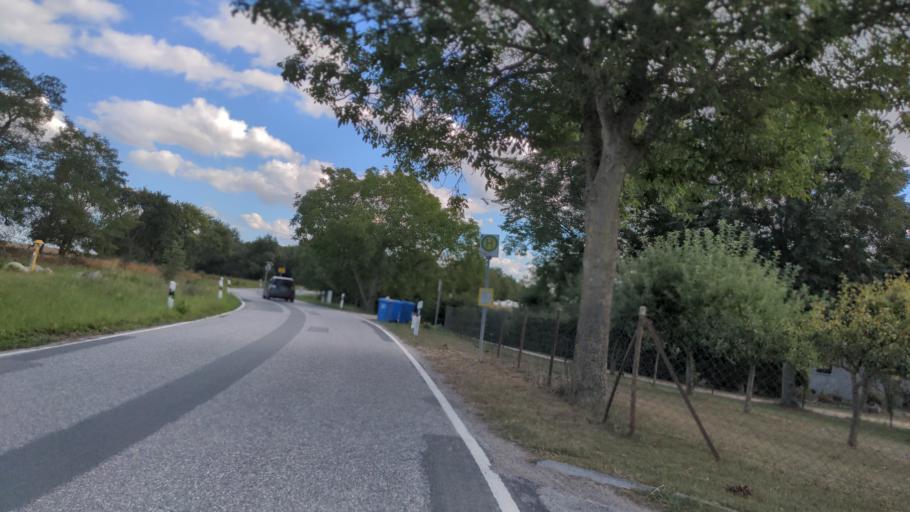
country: DE
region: Mecklenburg-Vorpommern
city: Gramkow
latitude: 53.9094
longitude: 11.3747
